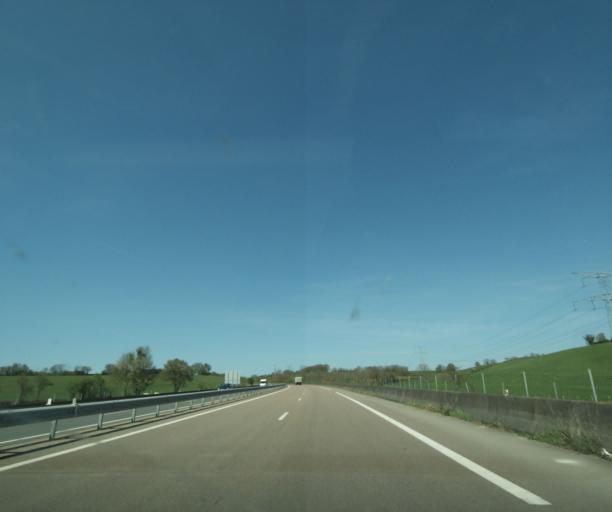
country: FR
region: Bourgogne
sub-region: Departement de la Nievre
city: Pougues-les-Eaux
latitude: 47.0799
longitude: 3.1232
